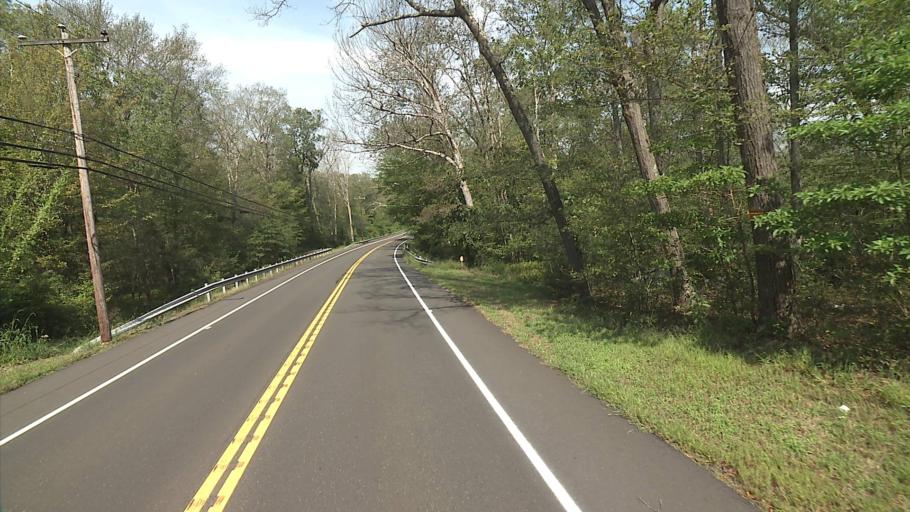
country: US
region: Connecticut
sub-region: Middlesex County
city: Durham
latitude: 41.3857
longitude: -72.6450
